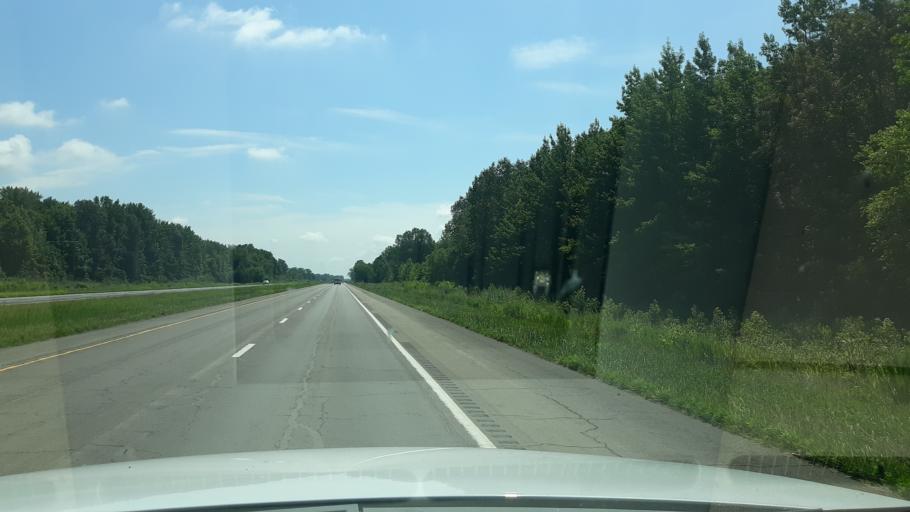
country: US
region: Illinois
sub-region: Saline County
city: Carrier Mills
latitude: 37.7333
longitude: -88.6656
